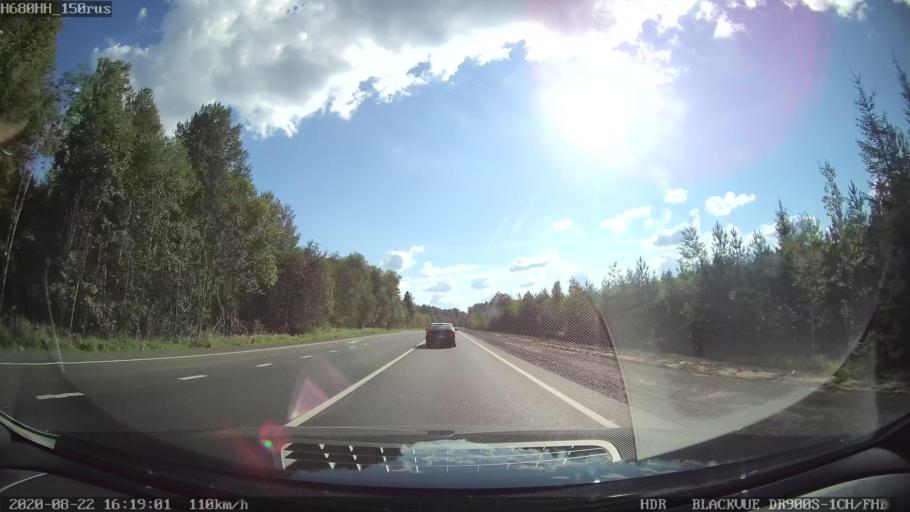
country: RU
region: Tverskaya
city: Rameshki
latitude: 57.4090
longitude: 36.1278
